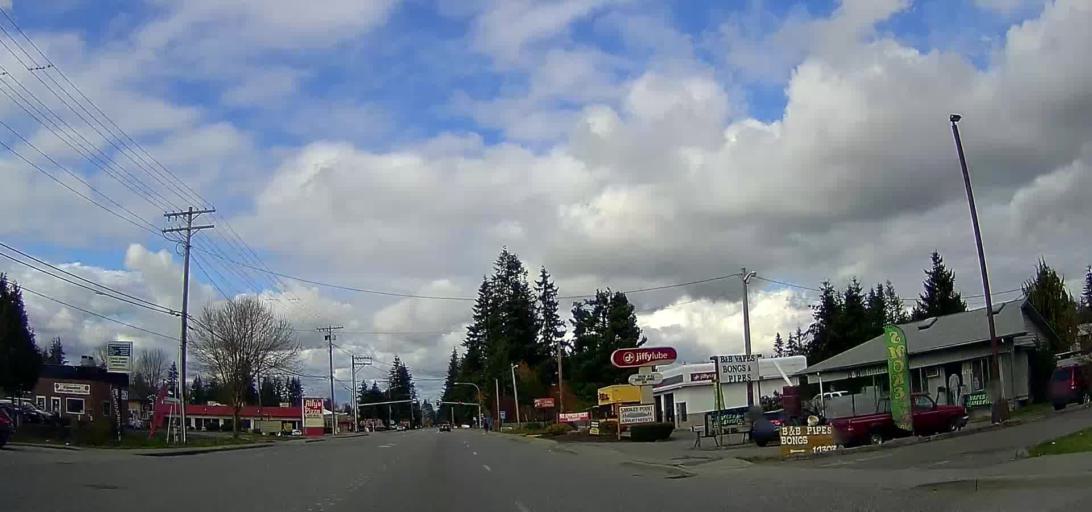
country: US
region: Washington
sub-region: Snohomish County
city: Smokey Point
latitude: 48.1532
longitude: -122.1830
